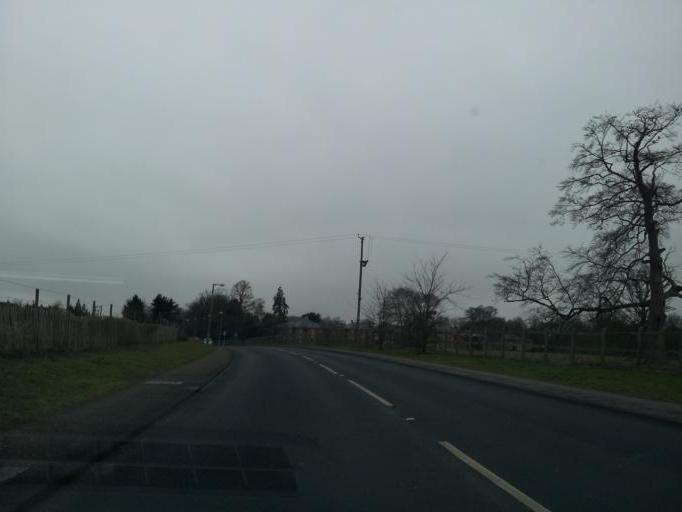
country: GB
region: England
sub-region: Essex
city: Manningtree
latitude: 51.9427
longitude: 1.0464
